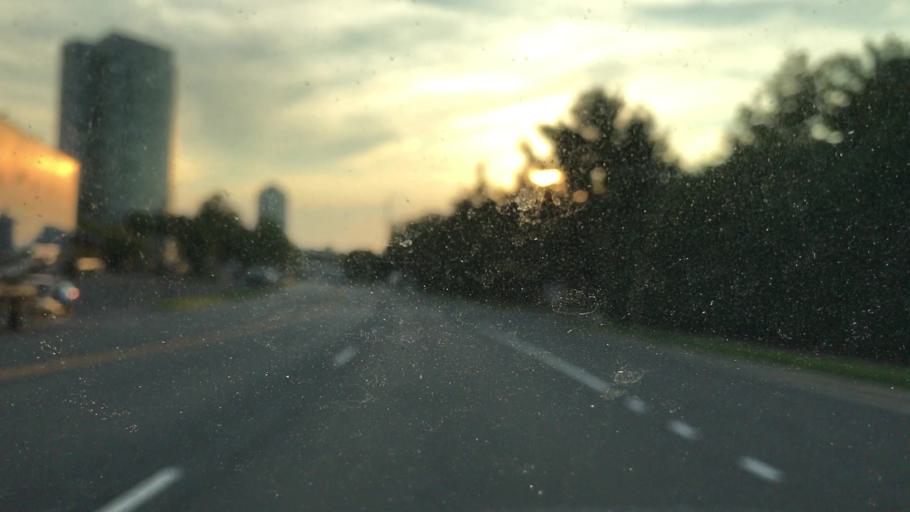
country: US
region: Virginia
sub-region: Fairfax County
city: Tysons Corner
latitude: 38.9313
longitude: -77.2355
